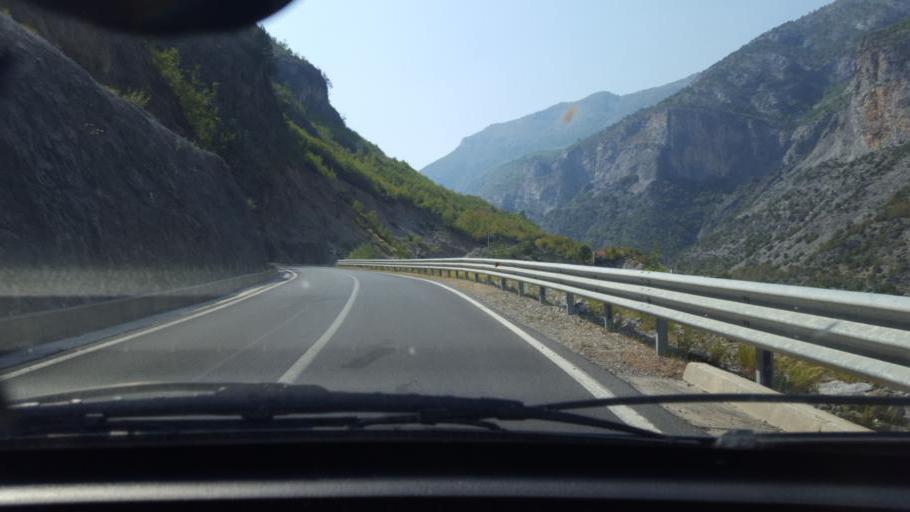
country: AL
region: Shkoder
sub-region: Rrethi i Malesia e Madhe
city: Kastrat
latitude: 42.4540
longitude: 19.5601
